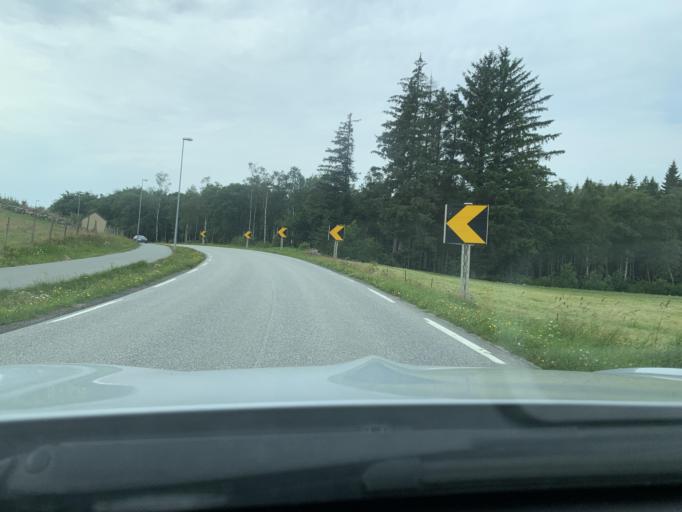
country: NO
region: Rogaland
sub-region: Time
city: Bryne
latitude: 58.7546
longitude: 5.7001
